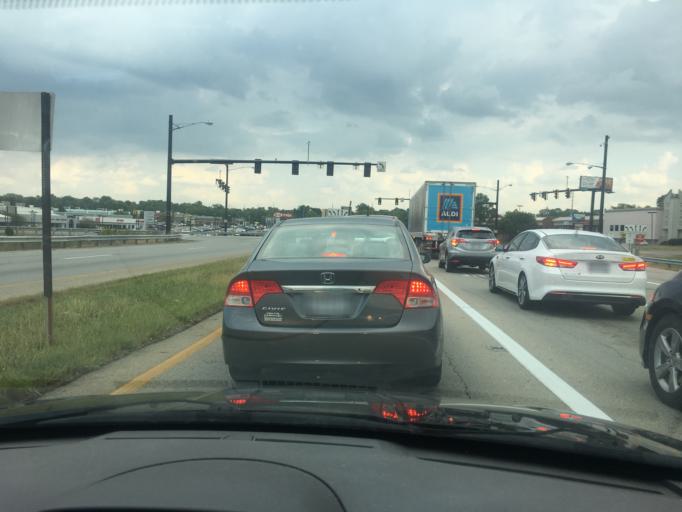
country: US
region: Ohio
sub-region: Clark County
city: Springfield
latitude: 39.9423
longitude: -83.8370
